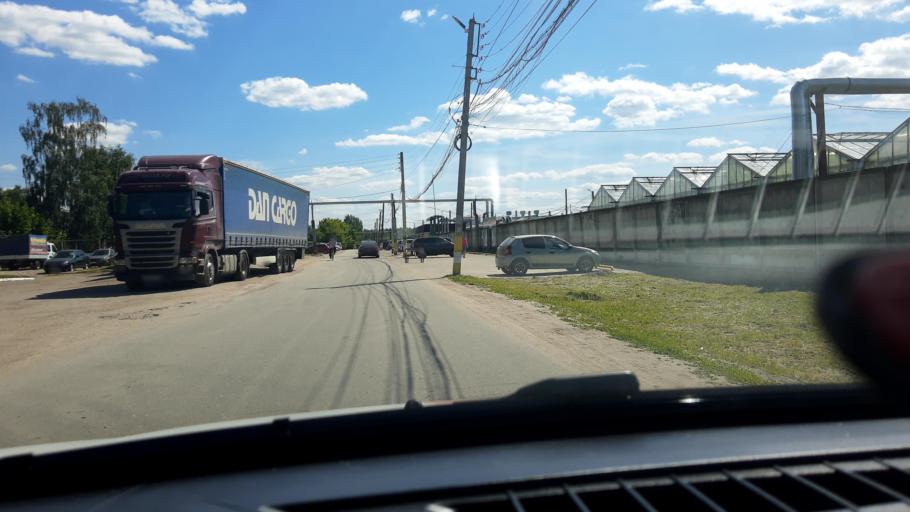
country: RU
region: Nizjnij Novgorod
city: Gorbatovka
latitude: 56.3084
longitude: 43.8134
